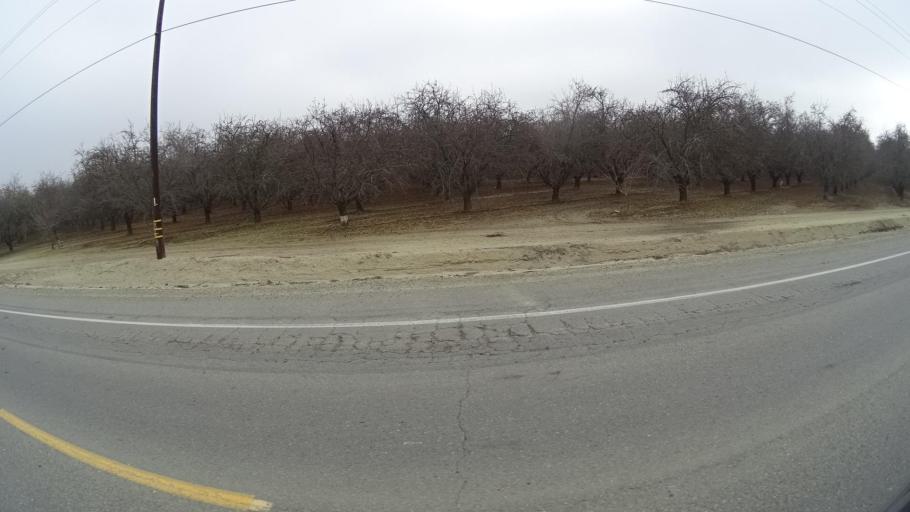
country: US
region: California
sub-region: Kern County
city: Greenfield
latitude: 35.0762
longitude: -119.1265
